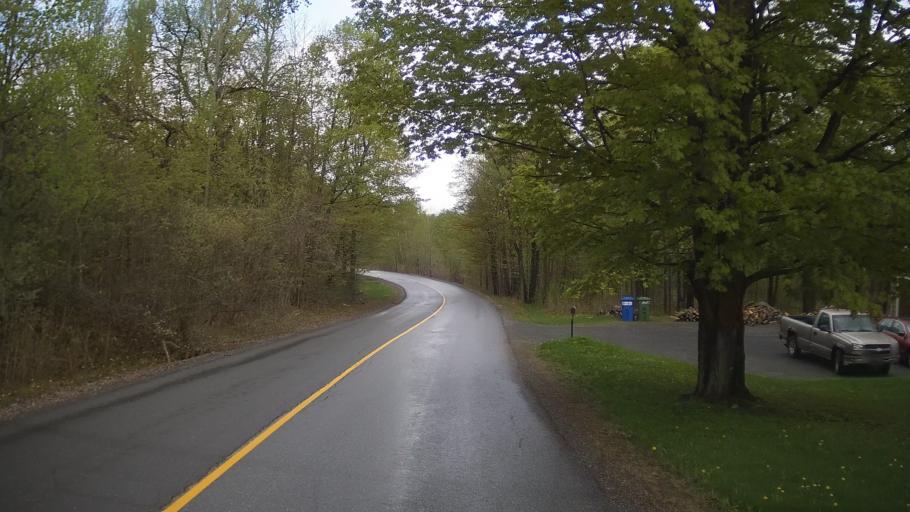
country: CA
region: Quebec
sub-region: Monteregie
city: Cowansville
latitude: 45.1977
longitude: -72.7071
